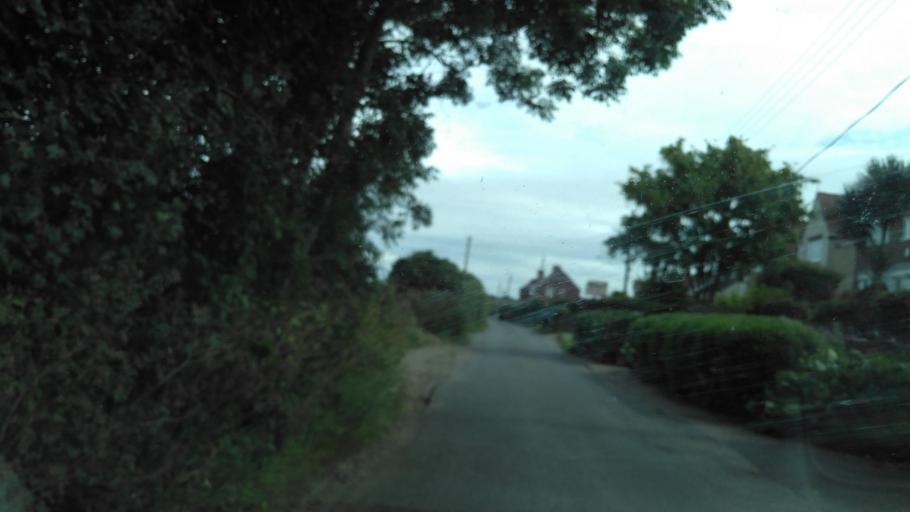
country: GB
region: England
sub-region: Kent
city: Canterbury
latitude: 51.2567
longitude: 1.0622
